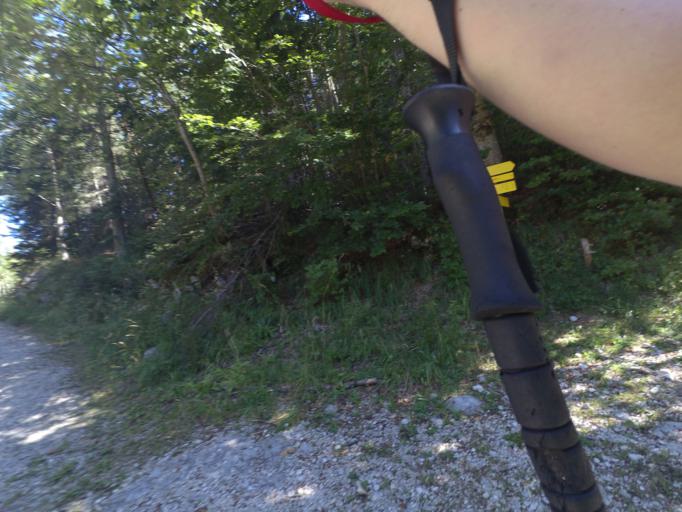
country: AT
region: Salzburg
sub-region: Politischer Bezirk Salzburg-Umgebung
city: Hintersee
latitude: 47.6982
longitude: 13.2469
